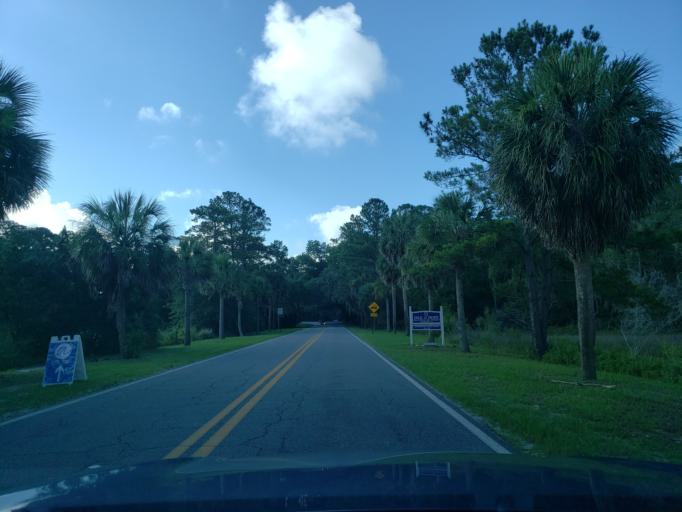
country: US
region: Georgia
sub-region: Chatham County
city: Isle of Hope
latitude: 31.9818
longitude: -81.0701
